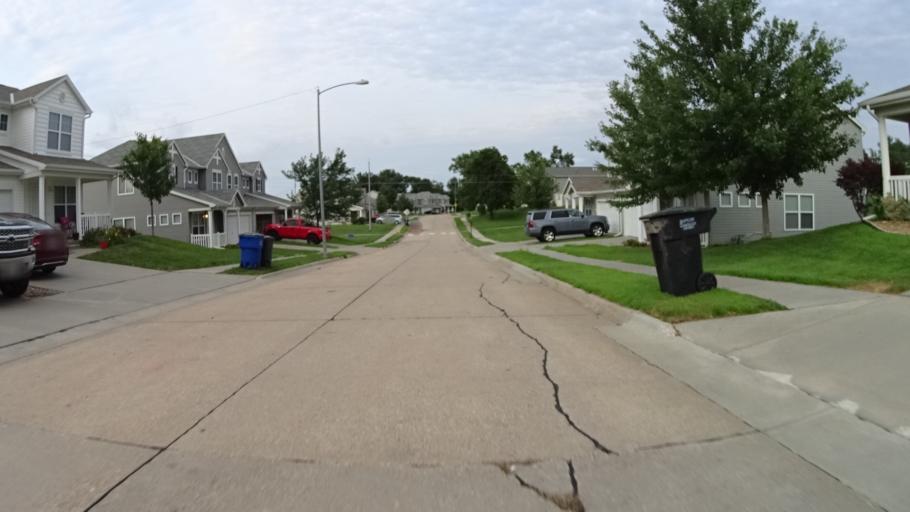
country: US
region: Nebraska
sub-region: Sarpy County
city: Offutt Air Force Base
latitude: 41.1251
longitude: -95.9504
